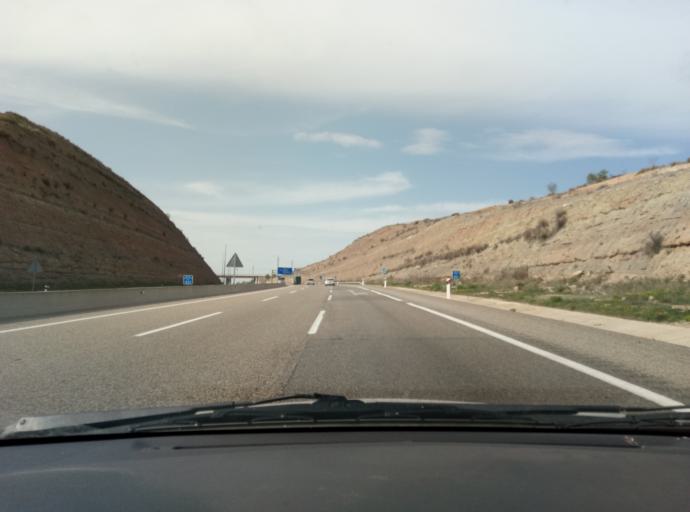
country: ES
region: Catalonia
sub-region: Provincia de Lleida
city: Cervera
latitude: 41.6735
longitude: 1.2910
